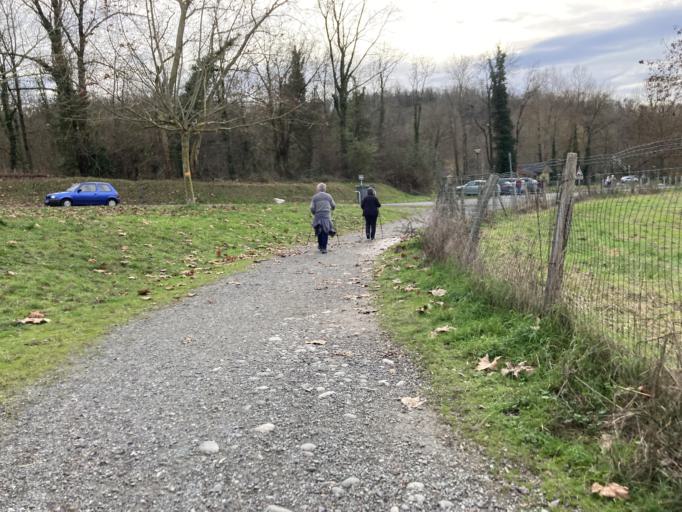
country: FR
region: Aquitaine
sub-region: Departement des Pyrenees-Atlantiques
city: Lescar
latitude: 43.3073
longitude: -0.4323
